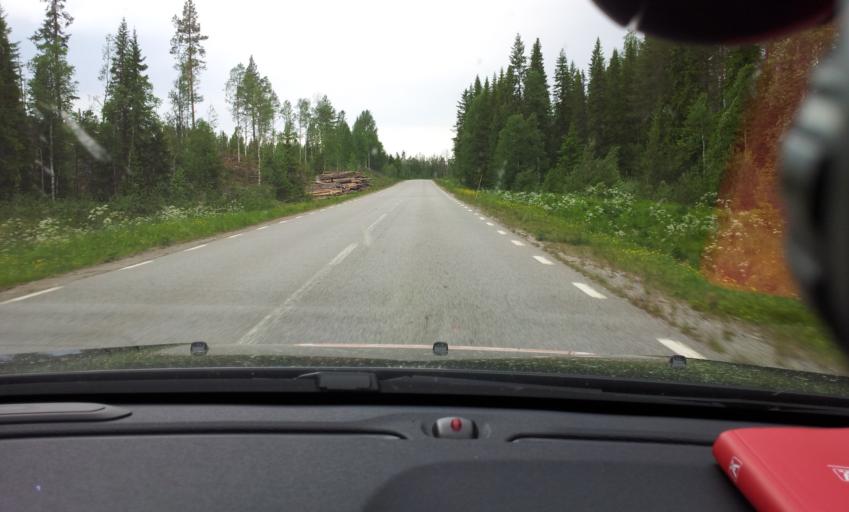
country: SE
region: Jaemtland
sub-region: Bergs Kommun
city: Hoverberg
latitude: 62.6831
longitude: 14.6437
